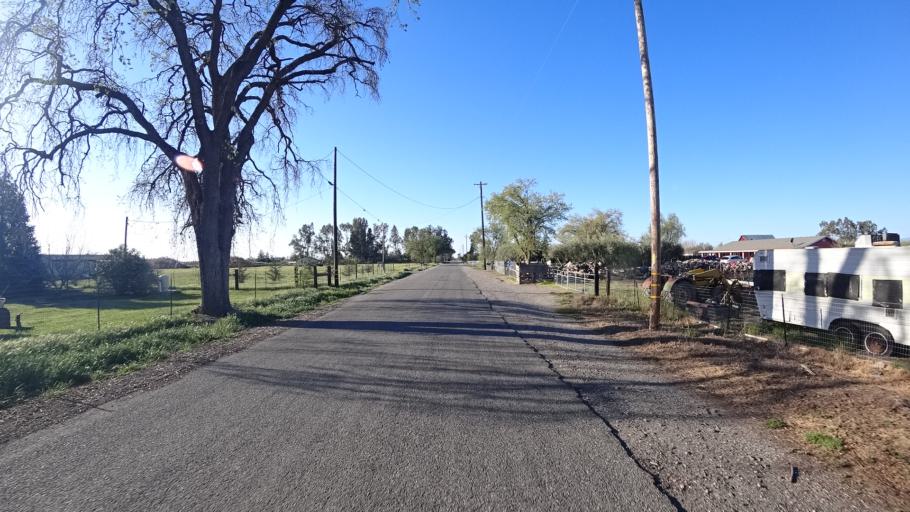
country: US
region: California
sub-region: Glenn County
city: Orland
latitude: 39.7684
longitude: -122.2297
